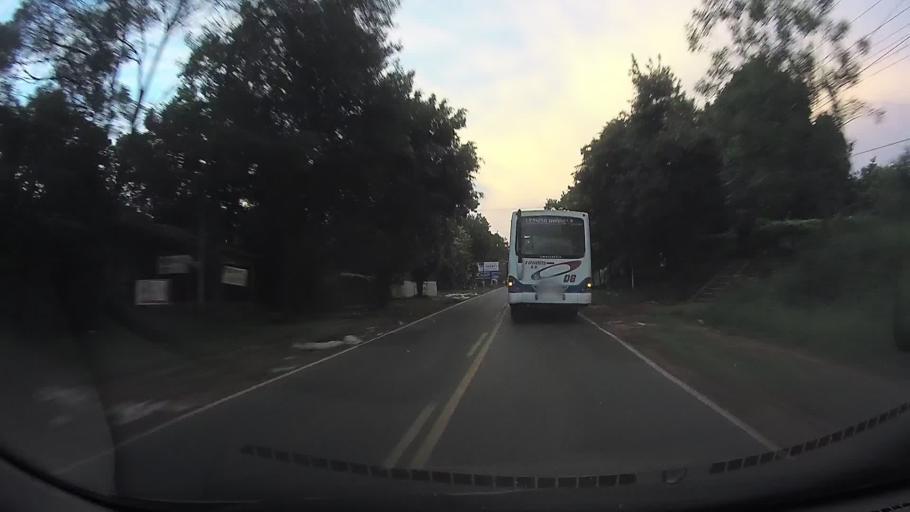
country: PY
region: Central
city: Ita
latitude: -25.4746
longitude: -57.3633
